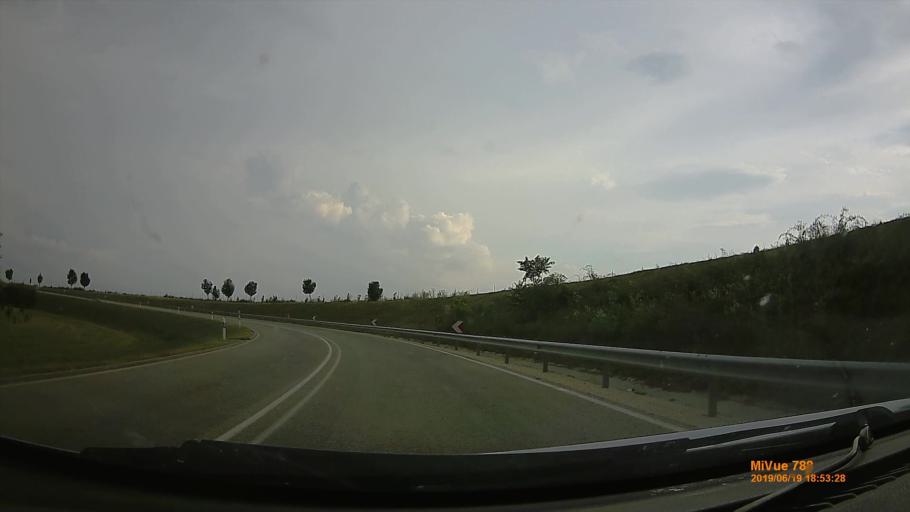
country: HU
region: Fejer
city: Rackeresztur
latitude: 47.3075
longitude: 18.8656
